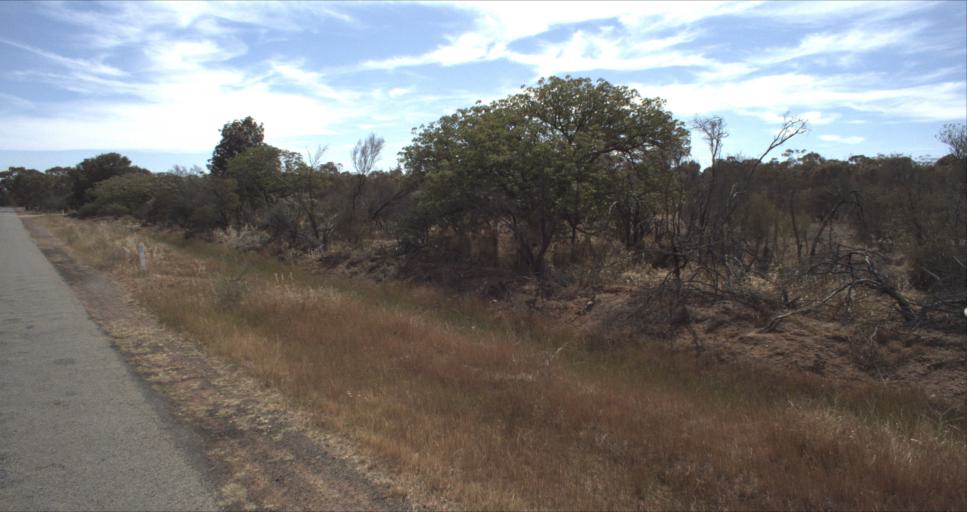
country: AU
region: New South Wales
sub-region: Leeton
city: Leeton
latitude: -34.5689
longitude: 146.4561
